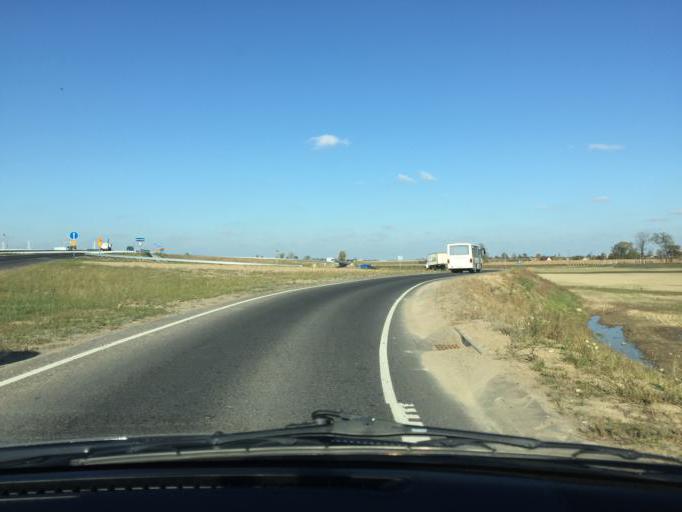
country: BY
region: Minsk
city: Slutsk
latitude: 53.0078
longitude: 27.4882
